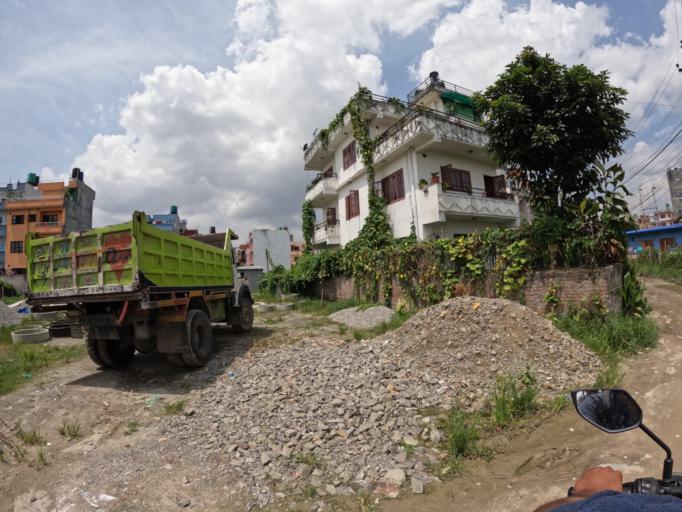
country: NP
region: Central Region
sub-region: Bagmati Zone
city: Kathmandu
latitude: 27.6792
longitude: 85.3718
